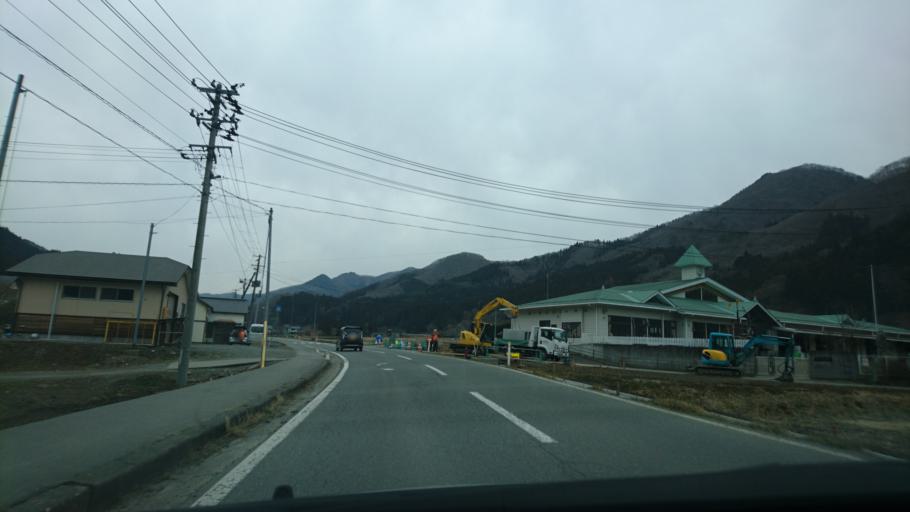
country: JP
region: Iwate
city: Tono
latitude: 39.1992
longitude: 141.5897
